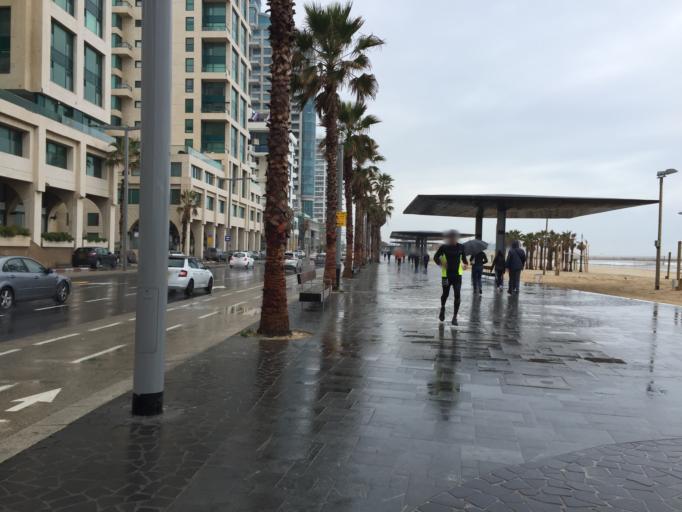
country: IL
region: Tel Aviv
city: Tel Aviv
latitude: 32.0724
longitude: 34.7644
